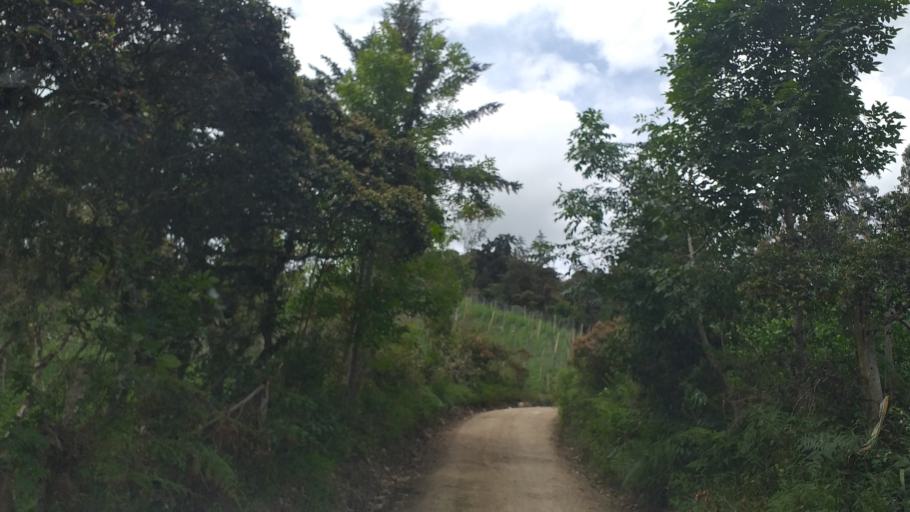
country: CO
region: Cundinamarca
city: Tenza
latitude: 5.0767
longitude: -73.4570
